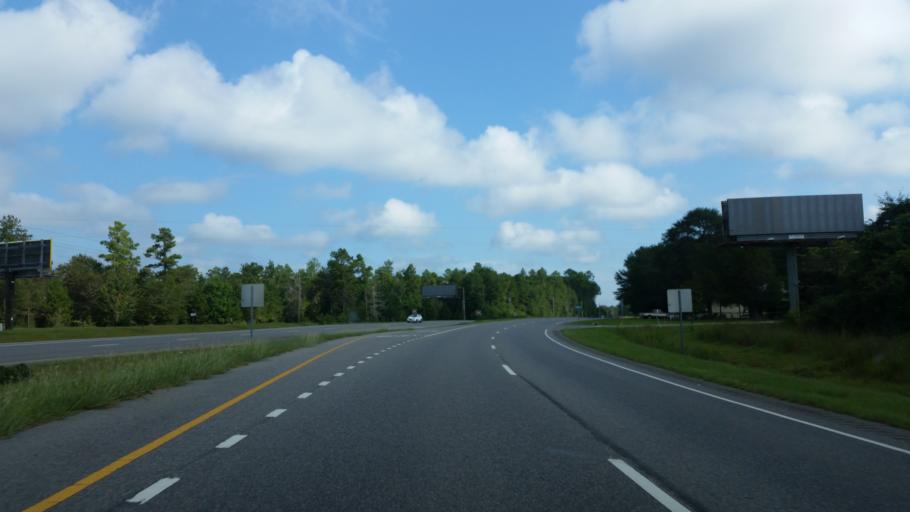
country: US
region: Alabama
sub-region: Baldwin County
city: Bay Minette
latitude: 30.9351
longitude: -87.7686
